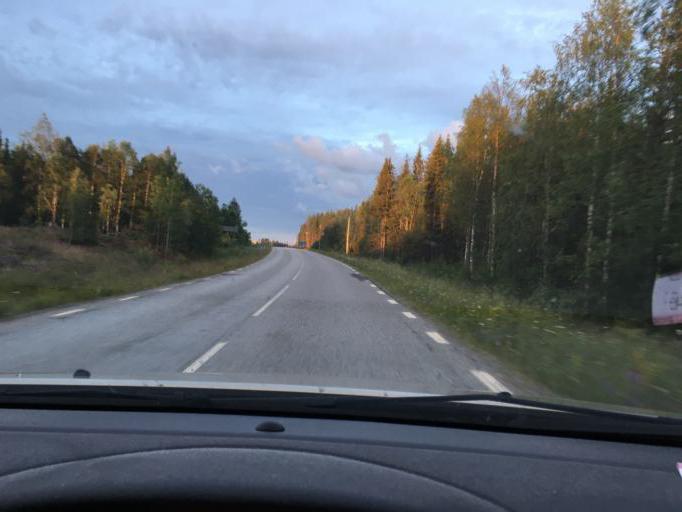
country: SE
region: Norrbotten
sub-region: Lulea Kommun
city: Ranea
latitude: 66.0429
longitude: 22.2929
